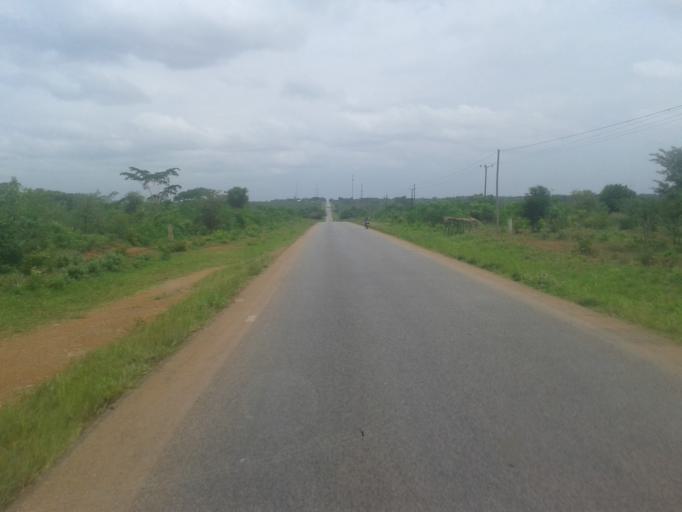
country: UG
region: Western Region
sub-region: Kiryandongo District
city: Masindi Port
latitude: 1.5014
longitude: 32.1204
